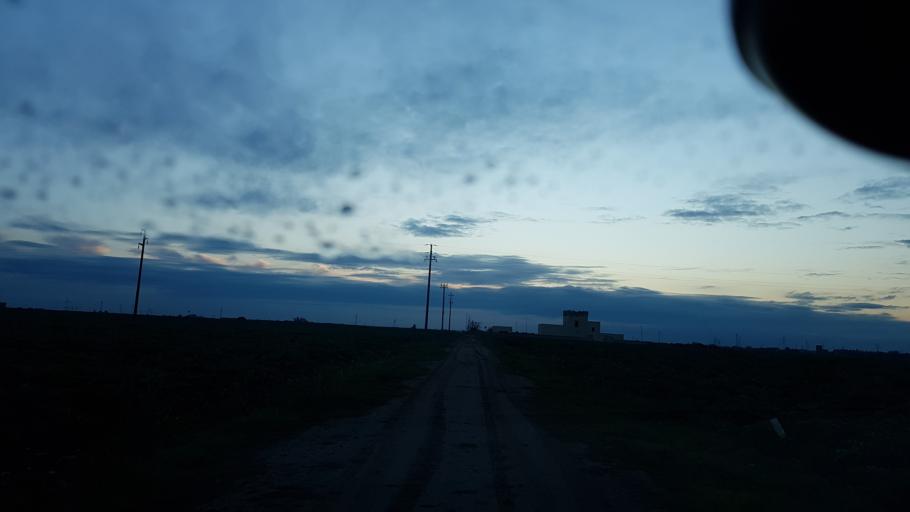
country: IT
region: Apulia
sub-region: Provincia di Brindisi
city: La Rosa
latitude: 40.6058
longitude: 18.0072
